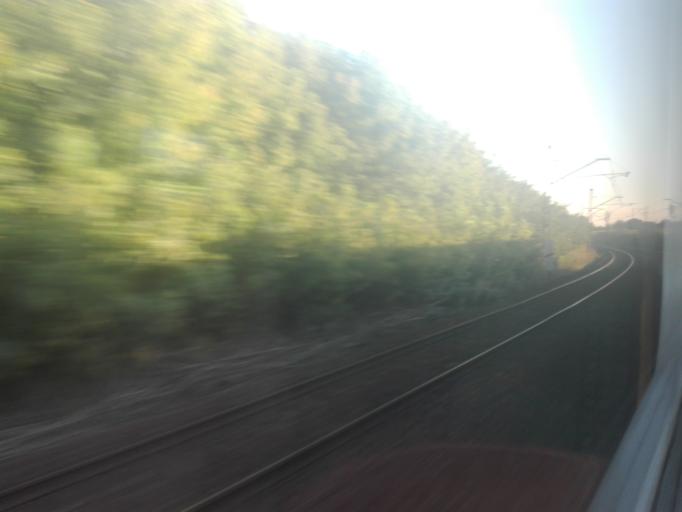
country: PL
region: Masovian Voivodeship
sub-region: Warszawa
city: Wlochy
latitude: 52.2143
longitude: 20.9412
